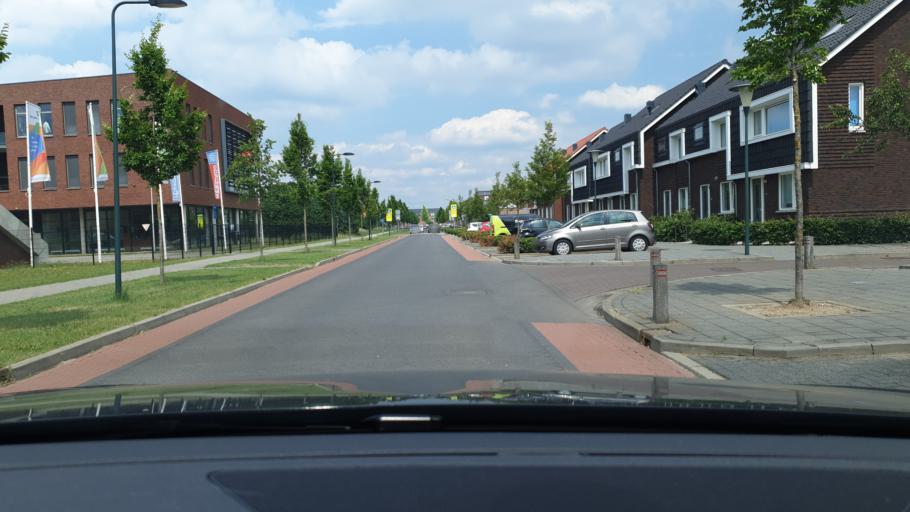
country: NL
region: Gelderland
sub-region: Gemeente Overbetuwe
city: Elst
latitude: 51.9178
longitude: 5.8612
